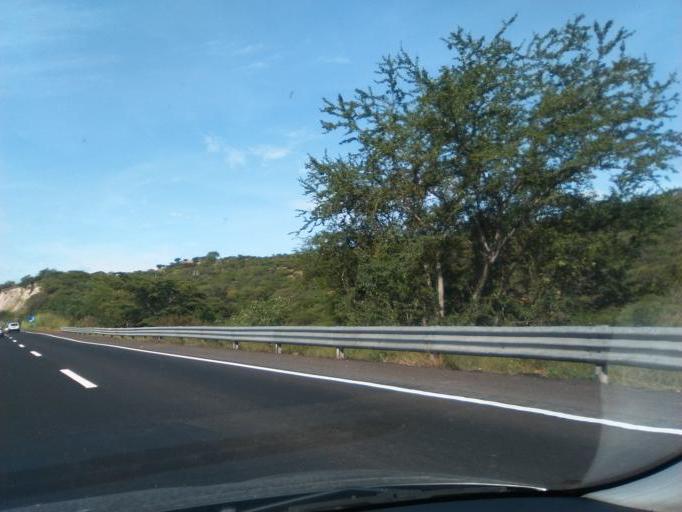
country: MX
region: Morelos
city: Tilzapotla
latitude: 18.4629
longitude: -99.1707
